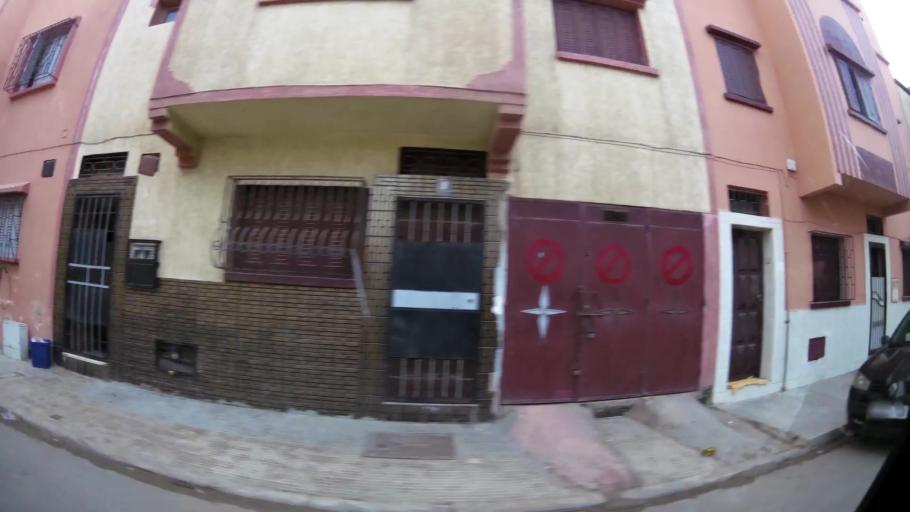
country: MA
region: Doukkala-Abda
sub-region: El-Jadida
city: El Jadida
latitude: 33.2492
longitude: -8.5274
